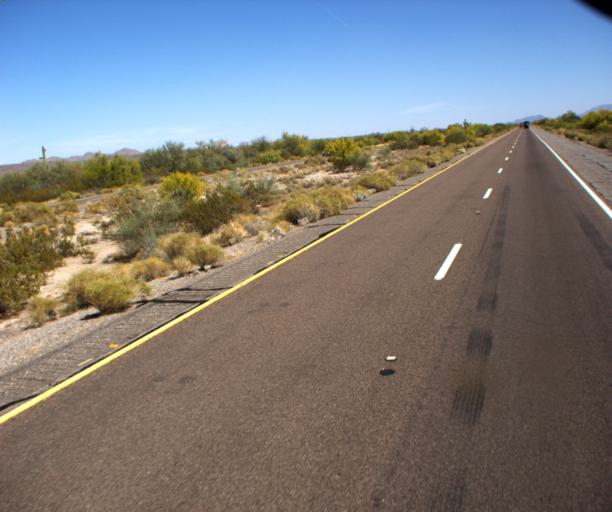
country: US
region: Arizona
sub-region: Maricopa County
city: Gila Bend
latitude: 32.8583
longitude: -112.3876
